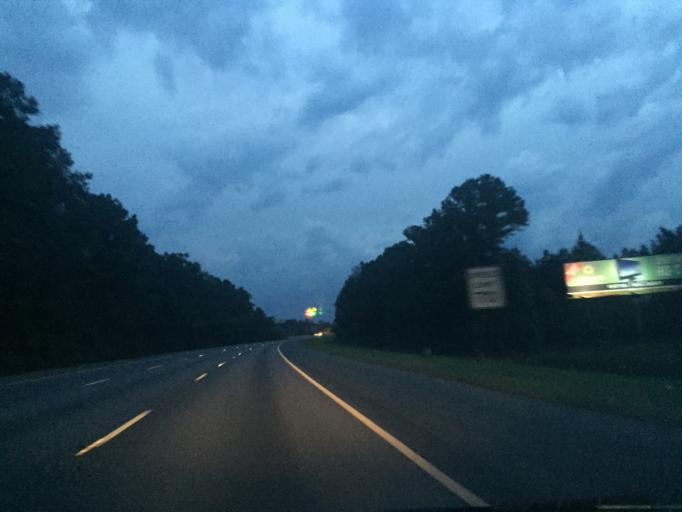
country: US
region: Georgia
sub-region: Bryan County
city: Richmond Hill
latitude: 31.9520
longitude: -81.3348
